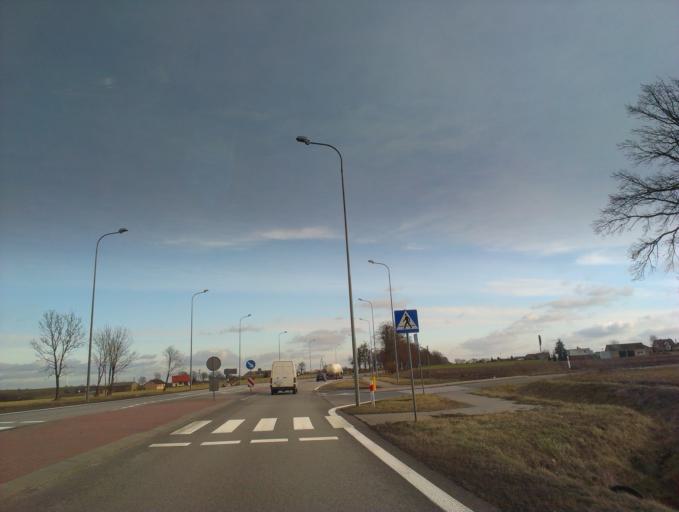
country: PL
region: Kujawsko-Pomorskie
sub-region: Powiat lipnowski
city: Kikol
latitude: 52.9341
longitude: 19.0589
